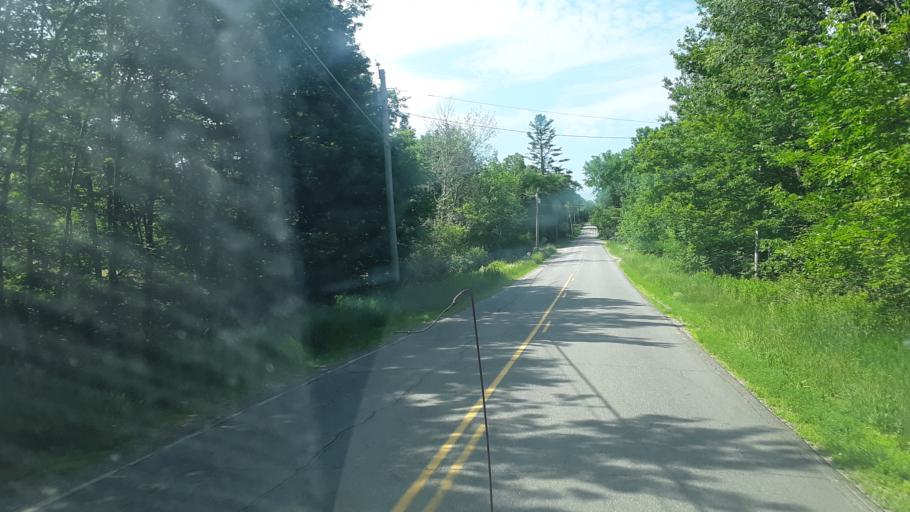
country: US
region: Maine
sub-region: Waldo County
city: Swanville
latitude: 44.5783
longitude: -68.9483
